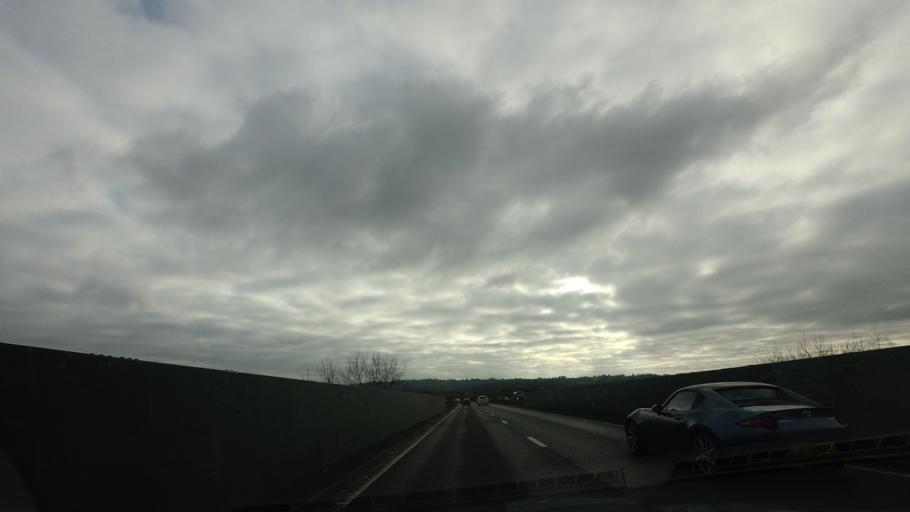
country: GB
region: England
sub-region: Kent
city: Tonbridge
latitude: 51.1920
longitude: 0.2343
